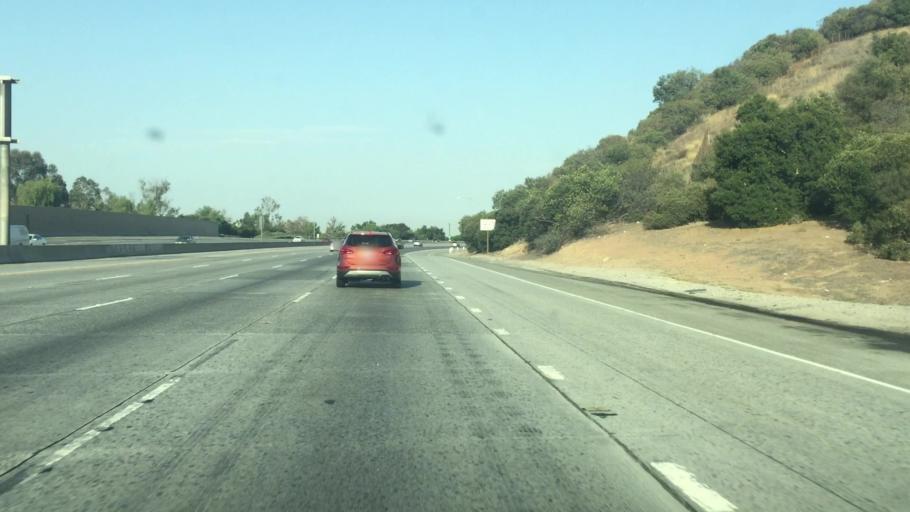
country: US
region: California
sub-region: Los Angeles County
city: Charter Oak
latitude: 34.1190
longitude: -117.8407
